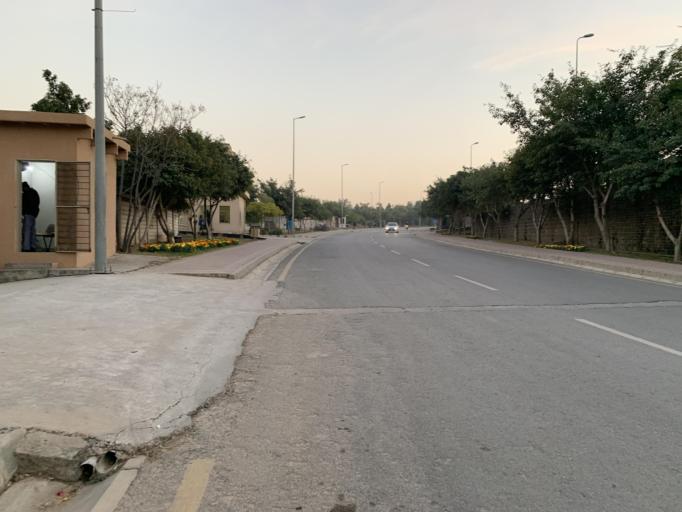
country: PK
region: Punjab
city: Rawalpindi
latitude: 33.6448
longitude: 72.9939
